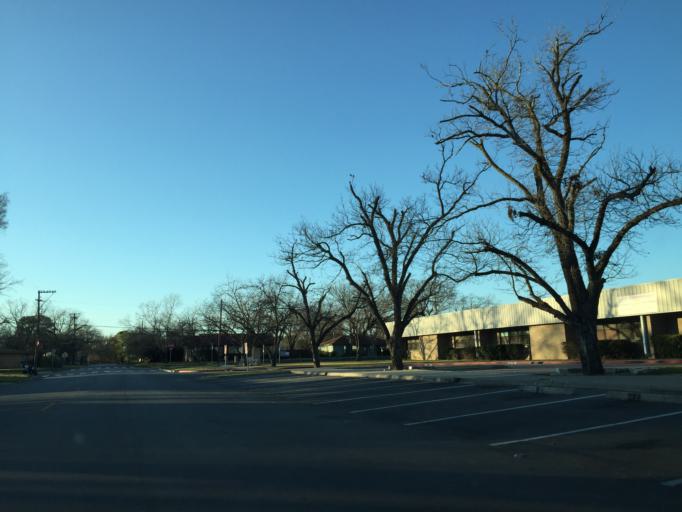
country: US
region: Texas
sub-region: Bastrop County
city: Elgin
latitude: 30.3491
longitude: -97.3802
